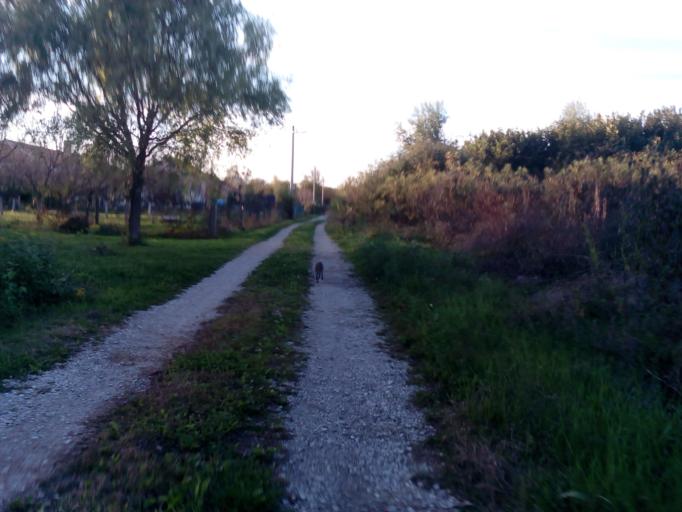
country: HR
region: Vukovarsko-Srijemska
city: Mirkovci
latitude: 45.2405
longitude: 18.8268
